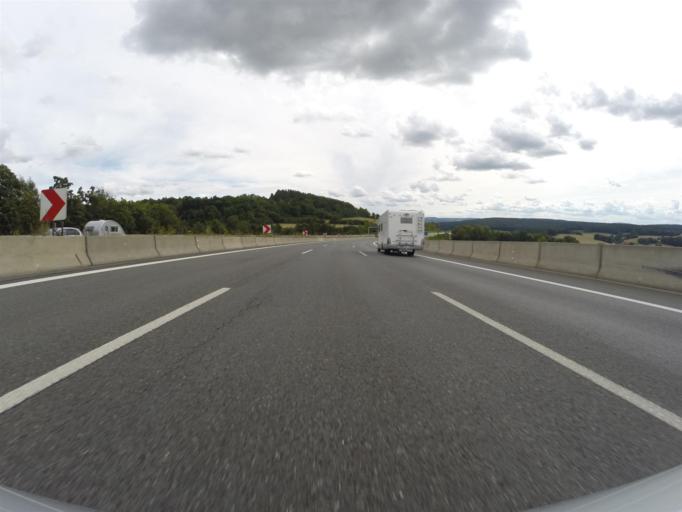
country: DE
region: Bavaria
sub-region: Upper Franconia
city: Bindlach
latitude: 50.0062
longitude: 11.6104
